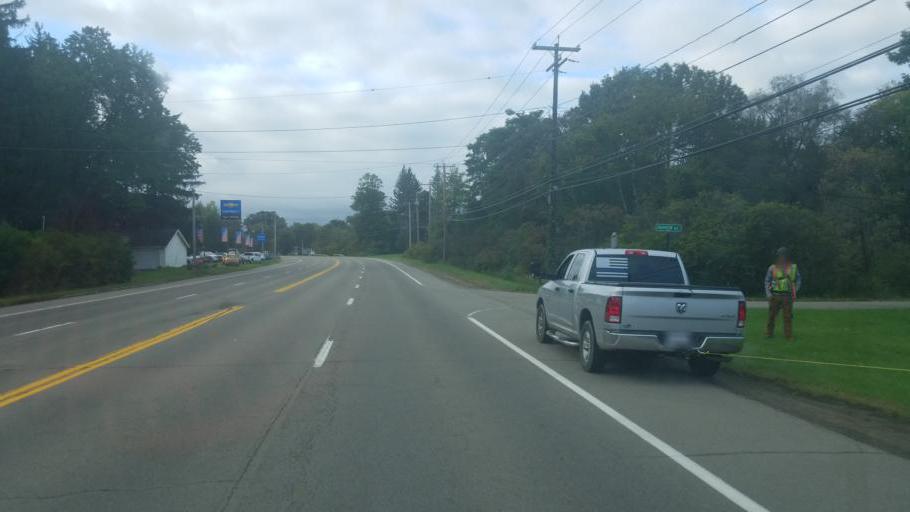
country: US
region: New York
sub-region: Cattaraugus County
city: Olean
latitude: 42.1230
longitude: -78.4142
